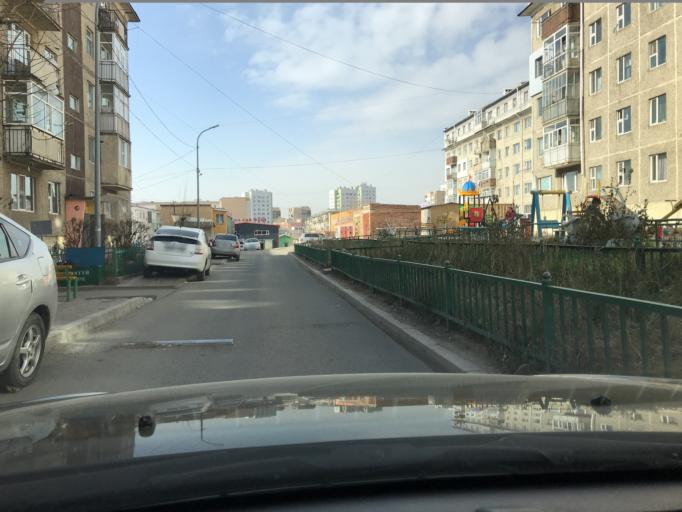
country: MN
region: Ulaanbaatar
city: Ulaanbaatar
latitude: 47.9223
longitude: 106.9471
